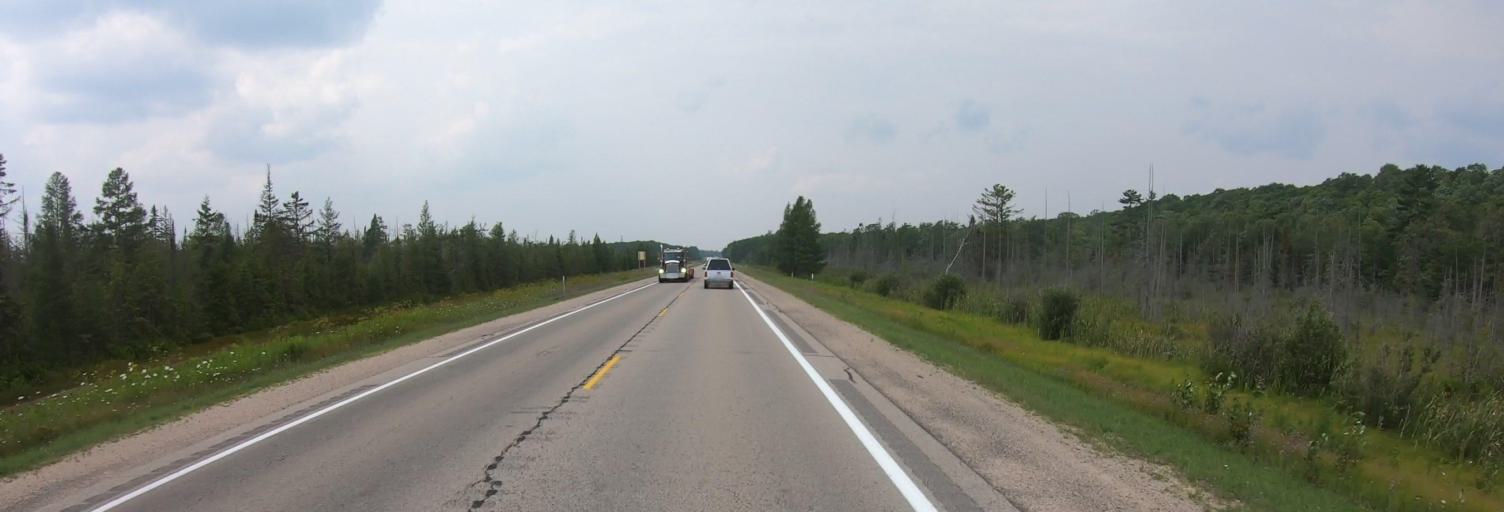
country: US
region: Michigan
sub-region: Alger County
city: Munising
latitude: 46.3761
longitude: -86.5674
